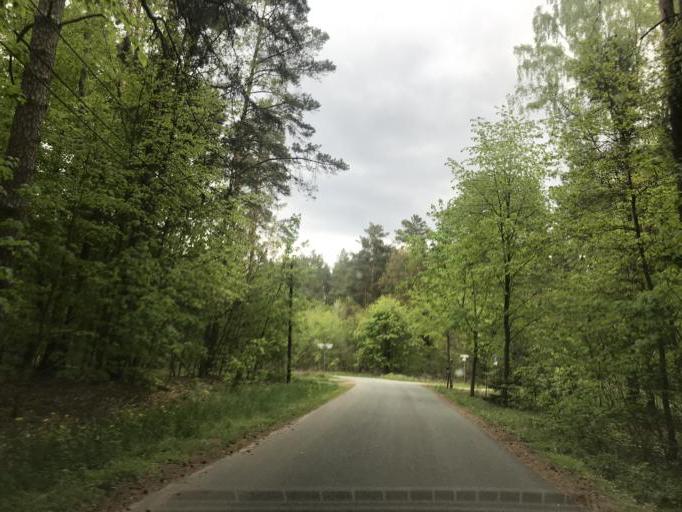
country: DE
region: Brandenburg
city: Rheinsberg
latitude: 53.0982
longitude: 12.8475
